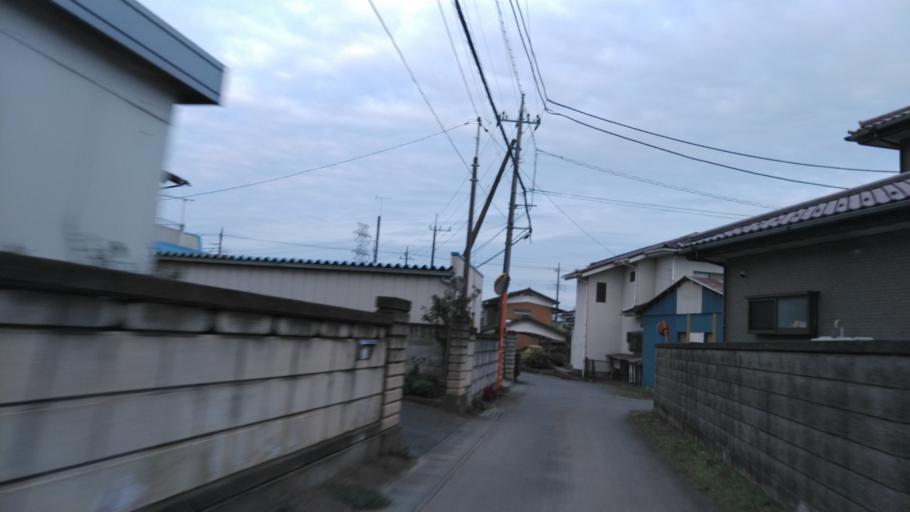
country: JP
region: Ibaraki
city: Yuki
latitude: 36.2722
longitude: 139.9117
